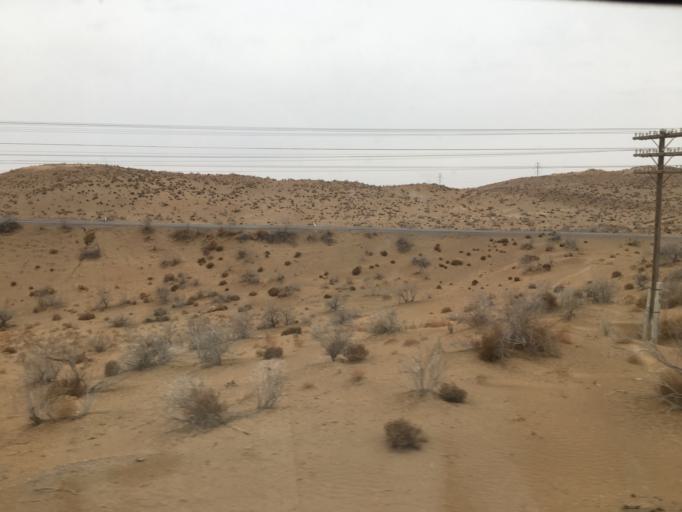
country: TM
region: Mary
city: Yoloeten
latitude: 36.4435
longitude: 62.5869
